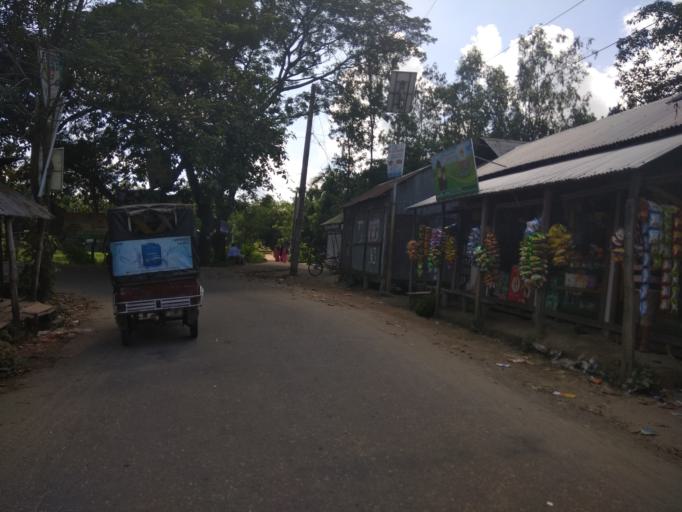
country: BD
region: Dhaka
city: Narayanganj
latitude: 23.4899
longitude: 90.4655
